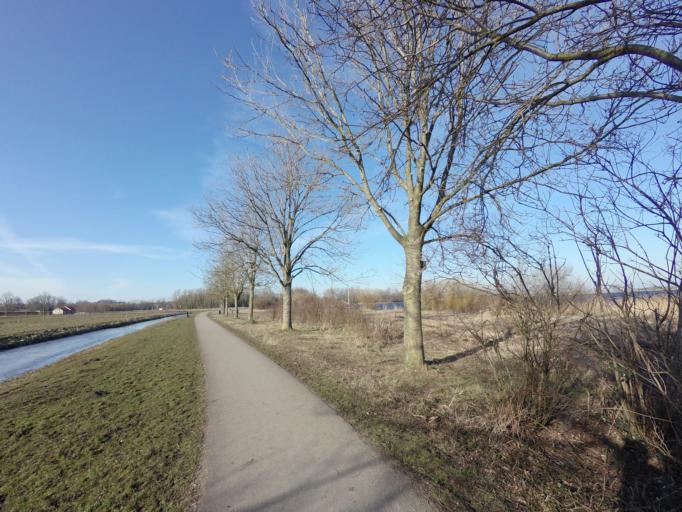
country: NL
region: South Holland
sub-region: Gemeente Leiden
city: Leiden
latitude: 52.1911
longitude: 4.5079
